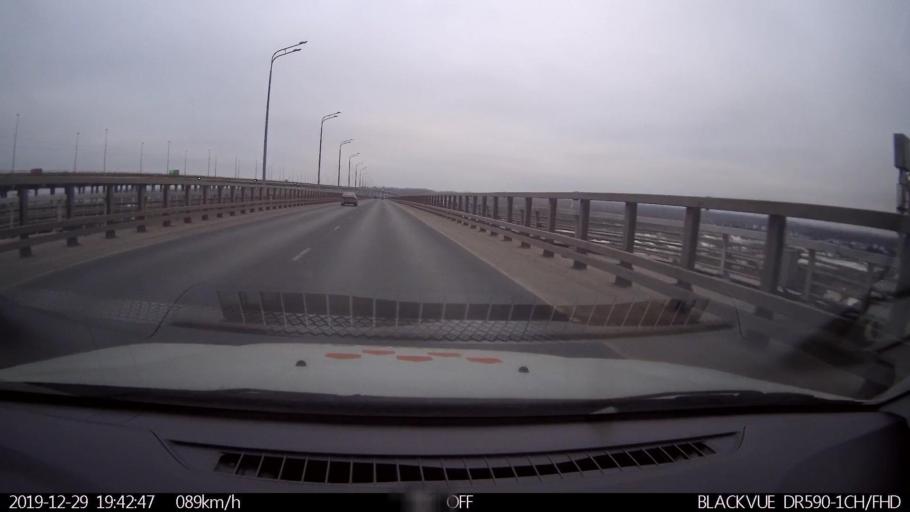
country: RU
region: Nizjnij Novgorod
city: Neklyudovo
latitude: 56.3544
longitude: 43.9263
